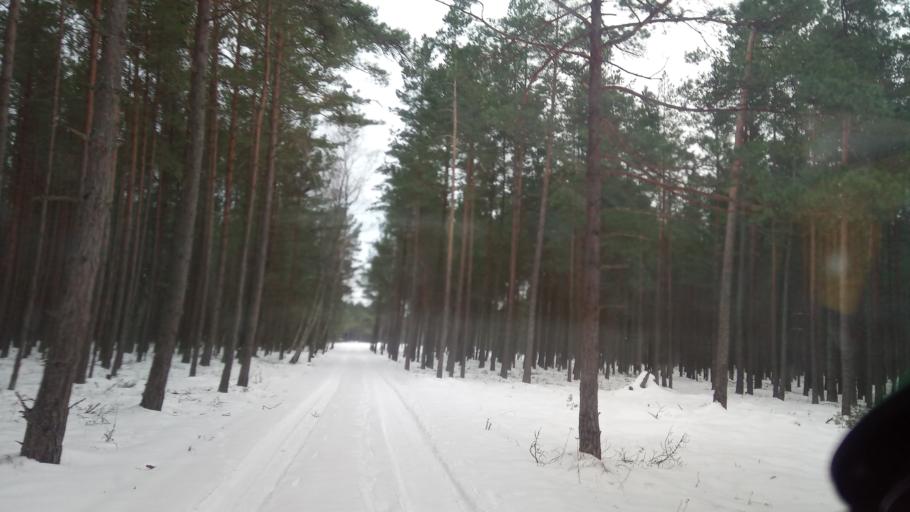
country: LT
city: Neringa
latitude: 55.4223
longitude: 21.0943
